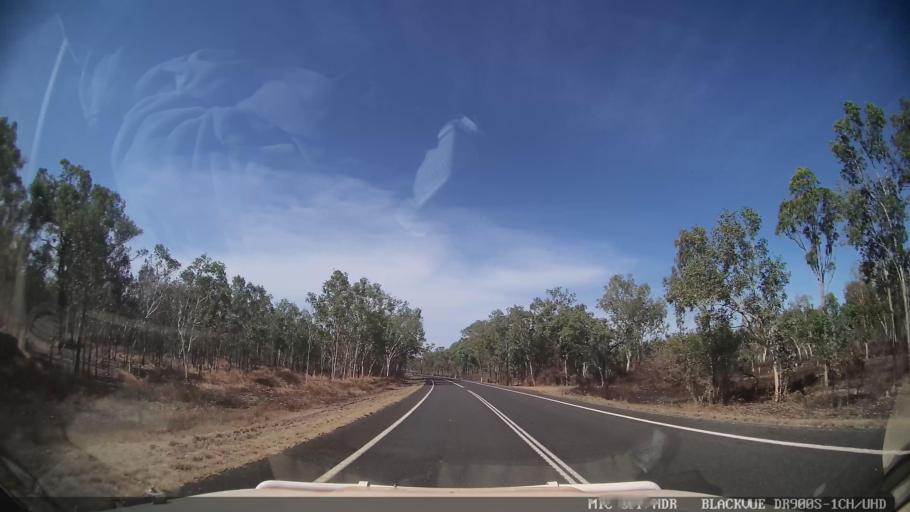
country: AU
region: Queensland
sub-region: Cook
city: Cooktown
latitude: -15.7881
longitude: 144.9511
